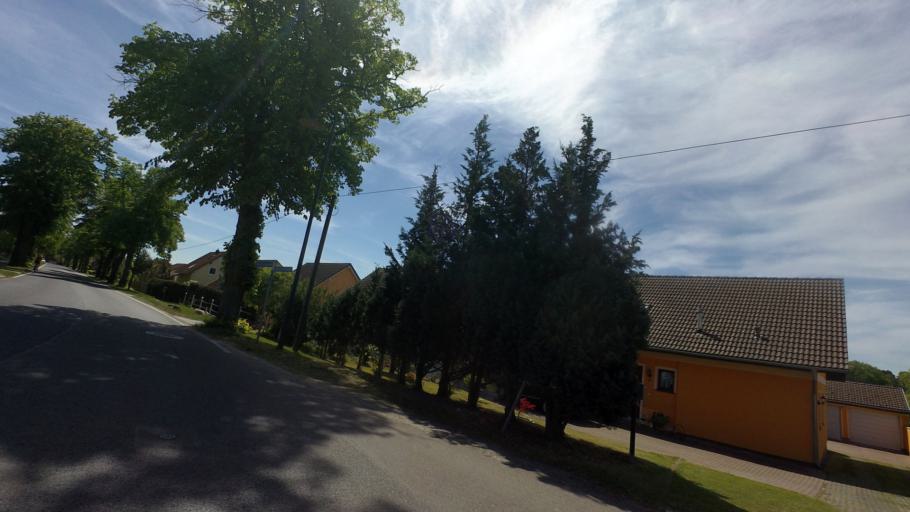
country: DE
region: Brandenburg
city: Luckenwalde
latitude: 52.1384
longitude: 13.1211
